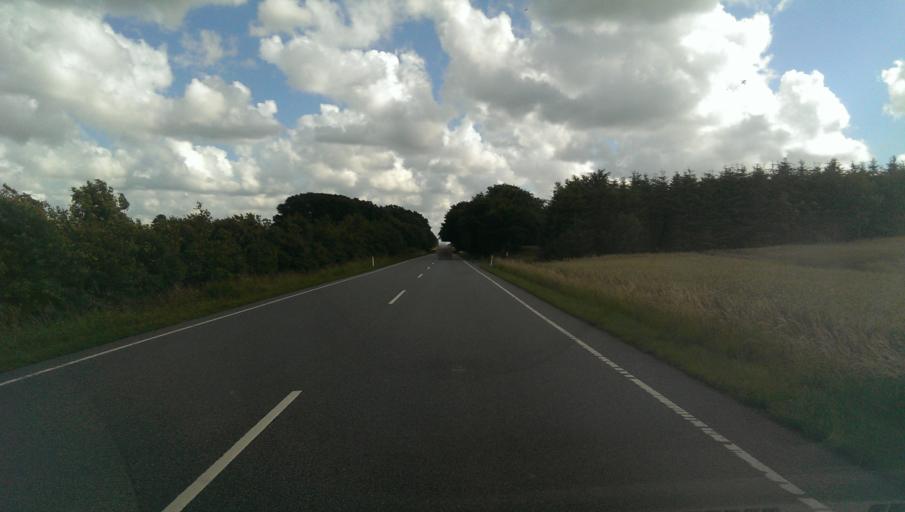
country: DK
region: South Denmark
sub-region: Varde Kommune
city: Varde
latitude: 55.6901
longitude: 8.4929
